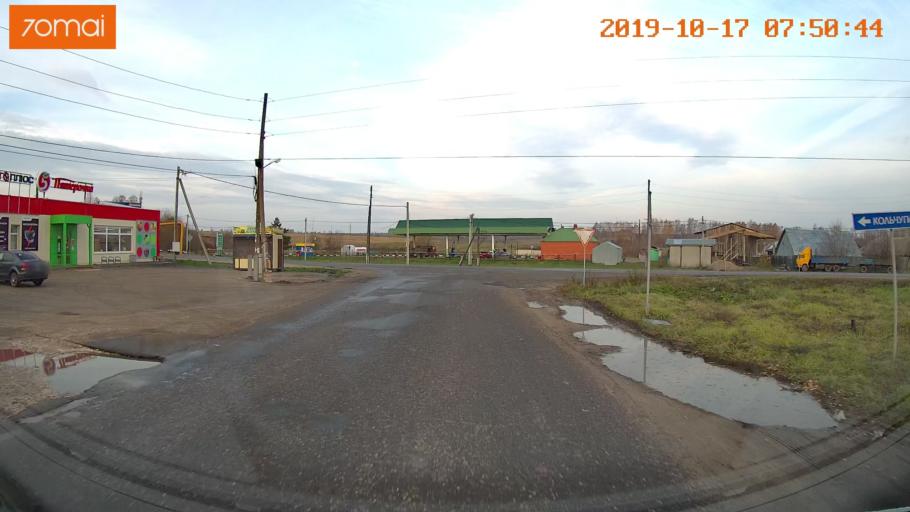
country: RU
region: Vladimir
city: Yur'yev-Pol'skiy
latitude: 56.4844
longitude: 39.6617
